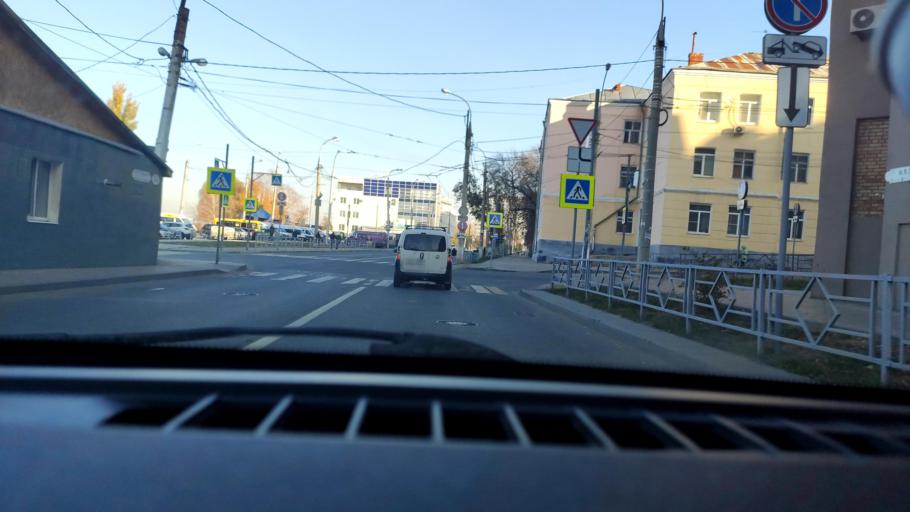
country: RU
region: Samara
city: Rozhdestveno
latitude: 53.1827
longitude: 50.0758
